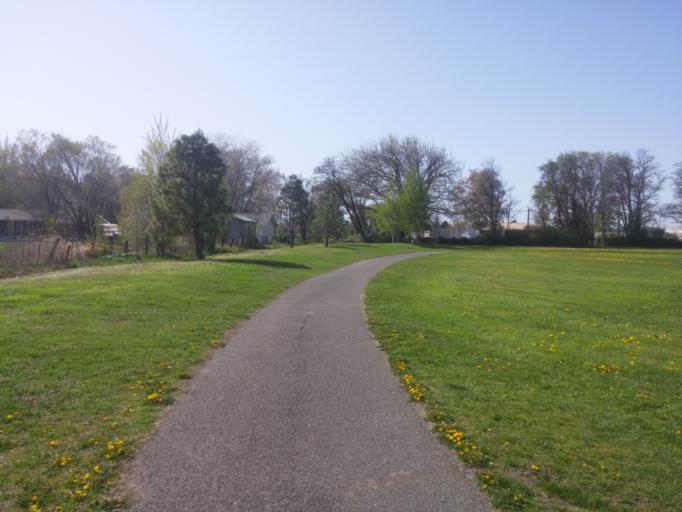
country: US
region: Washington
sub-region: Kittitas County
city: Ellensburg
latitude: 47.0094
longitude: -120.5248
